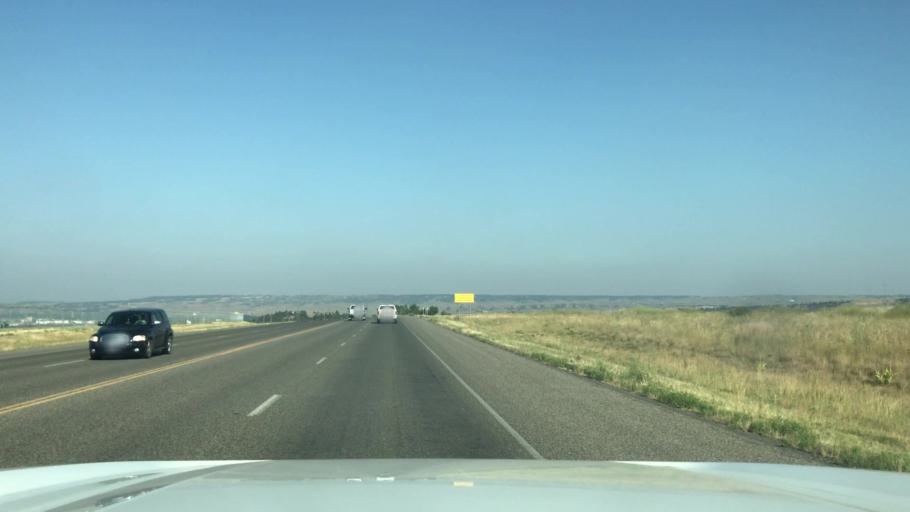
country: US
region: Montana
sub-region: Yellowstone County
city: Billings
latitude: 45.7997
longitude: -108.5136
